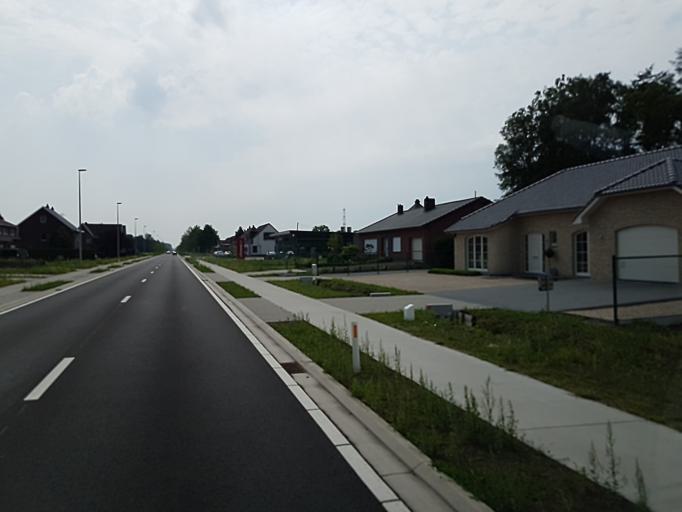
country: BE
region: Flanders
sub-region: Provincie Antwerpen
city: Balen
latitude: 51.1494
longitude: 5.2106
